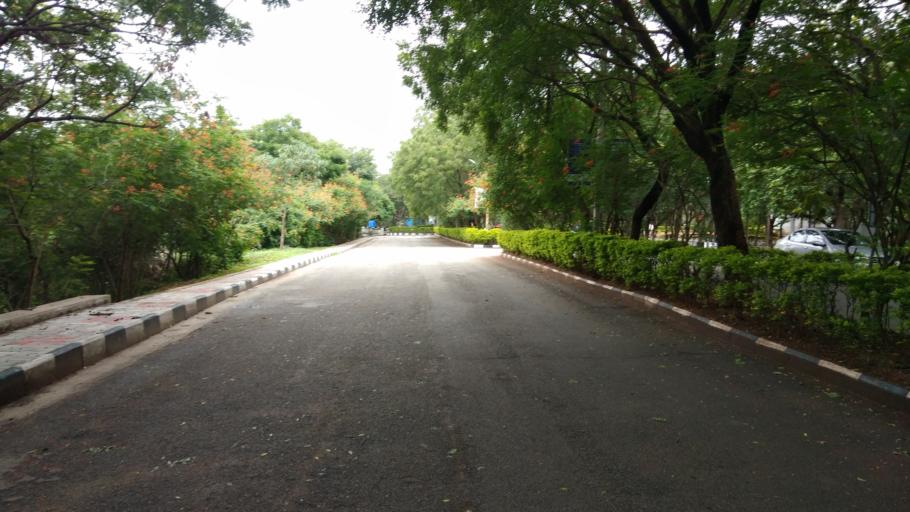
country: IN
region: Telangana
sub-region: Medak
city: Serilingampalle
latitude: 17.4464
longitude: 78.3503
